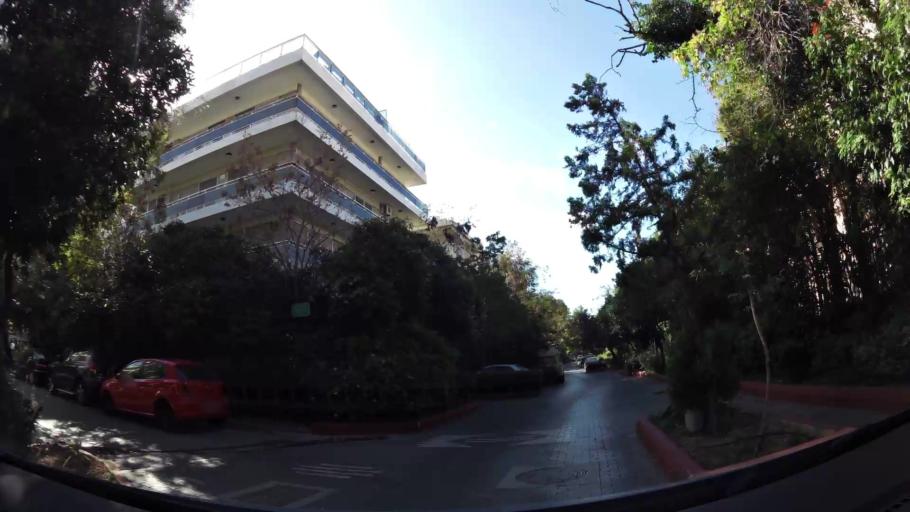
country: GR
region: Attica
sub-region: Nomarchia Athinas
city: Neo Psychiko
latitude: 38.0027
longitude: 23.7782
